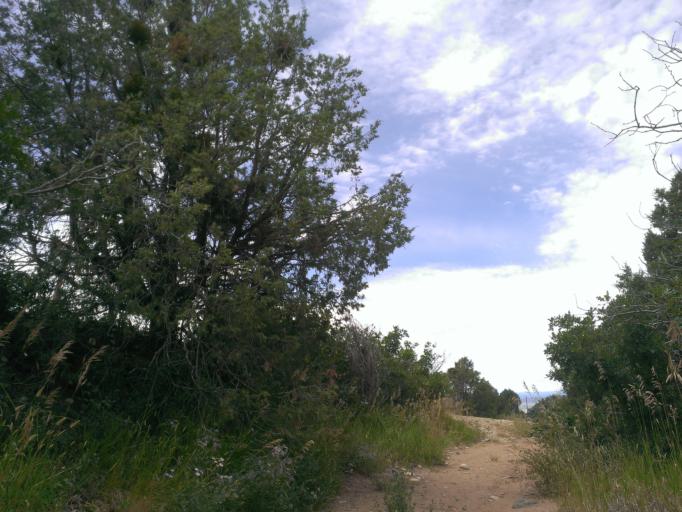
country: US
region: New Mexico
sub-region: Taos County
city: Arroyo Seco
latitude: 36.5345
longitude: -105.5599
